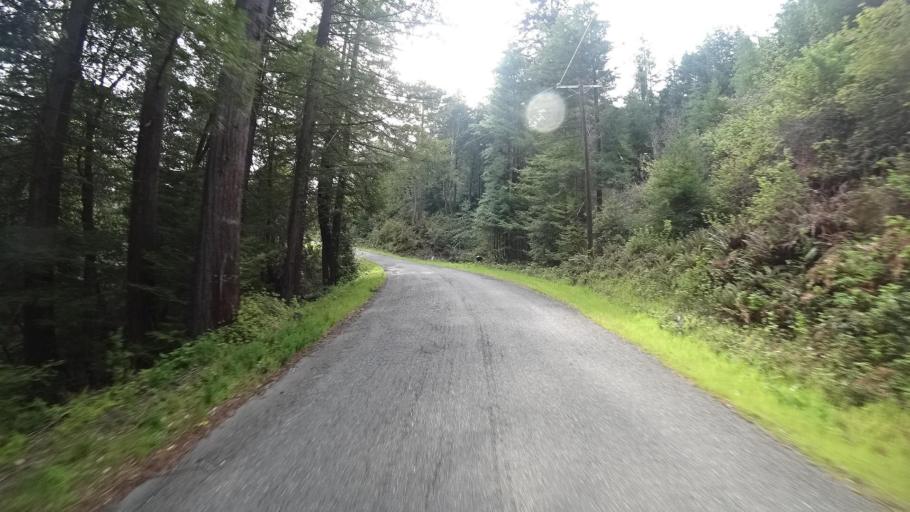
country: US
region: California
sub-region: Humboldt County
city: Redway
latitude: 40.3401
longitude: -123.8753
